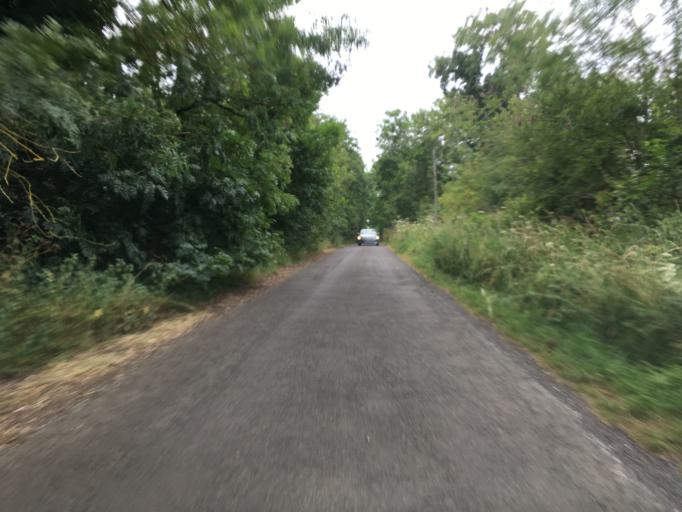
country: GB
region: England
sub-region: Oxfordshire
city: Hook Norton
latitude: 51.9452
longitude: -1.4476
